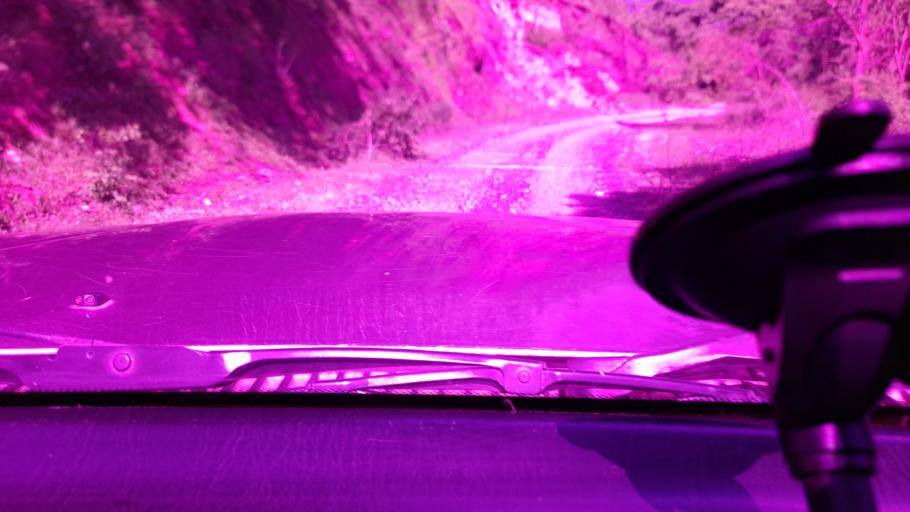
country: ET
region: Oromiya
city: Jima
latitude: 7.8061
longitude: 37.5262
